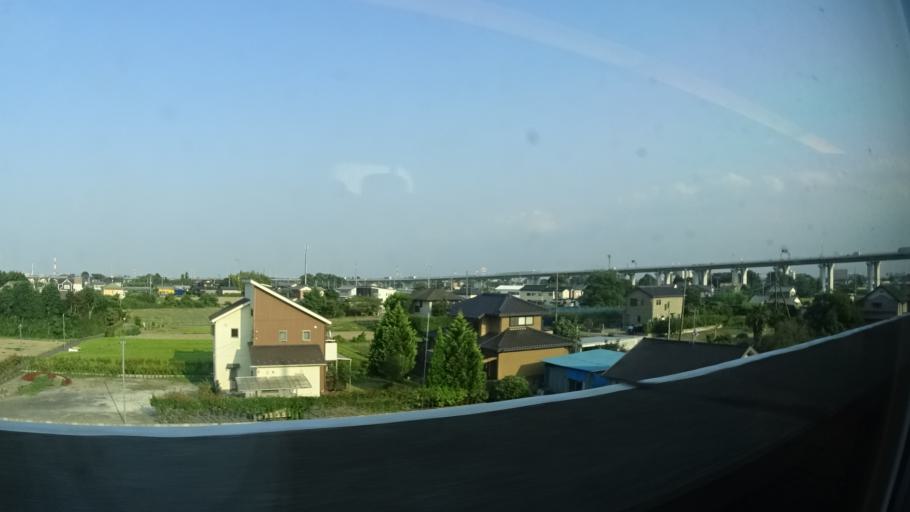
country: JP
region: Saitama
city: Kukichuo
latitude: 36.0495
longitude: 139.6698
